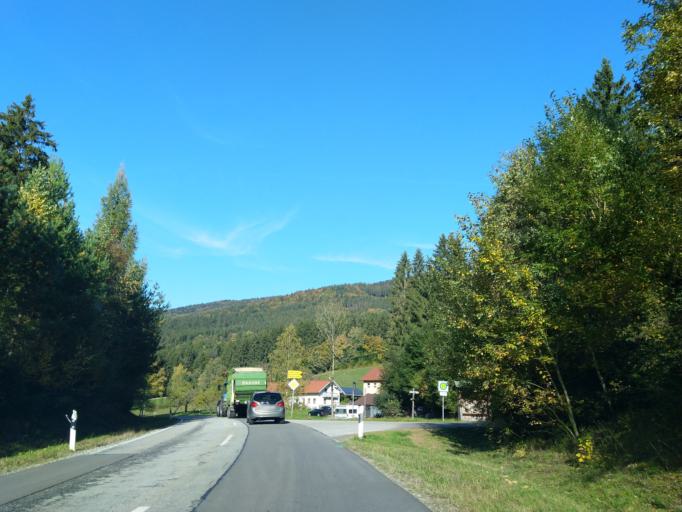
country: DE
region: Bavaria
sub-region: Lower Bavaria
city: Bernried
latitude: 48.9172
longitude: 12.9227
